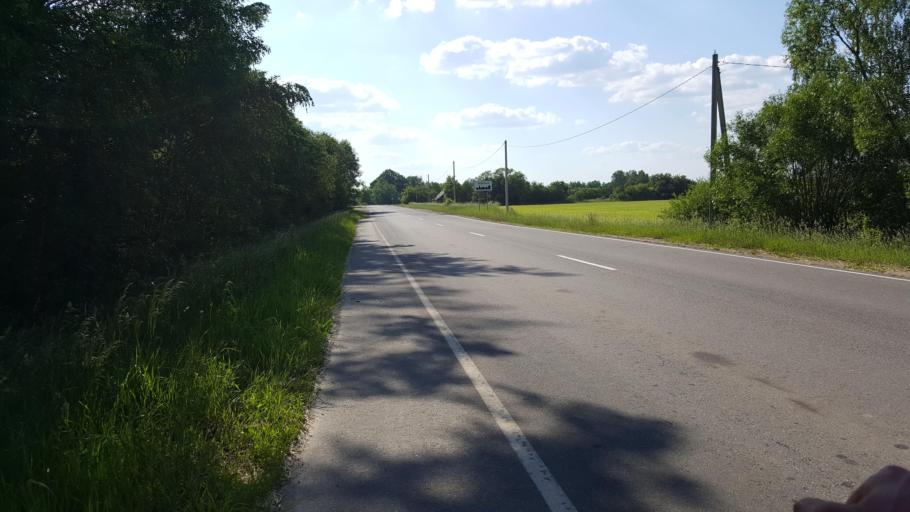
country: BY
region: Brest
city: Zhabinka
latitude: 52.3592
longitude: 24.1596
